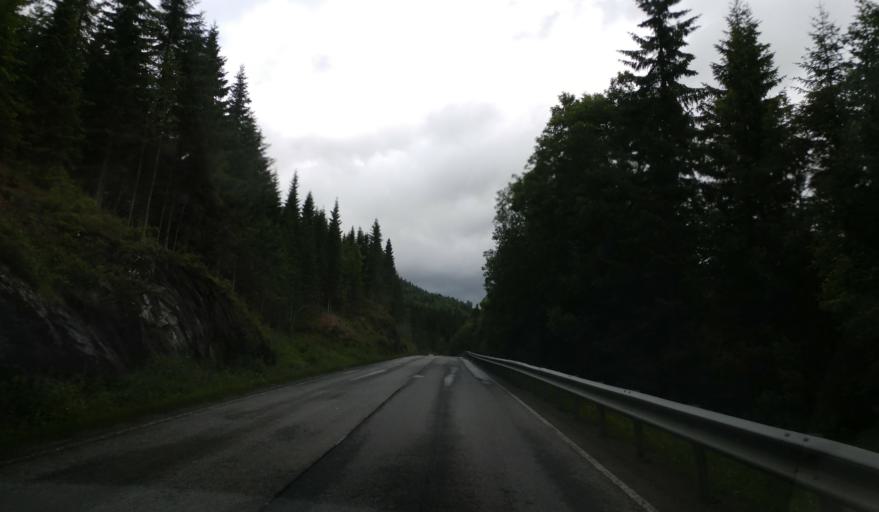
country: NO
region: Sor-Trondelag
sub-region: Selbu
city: Mebonden
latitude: 63.3026
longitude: 11.0787
